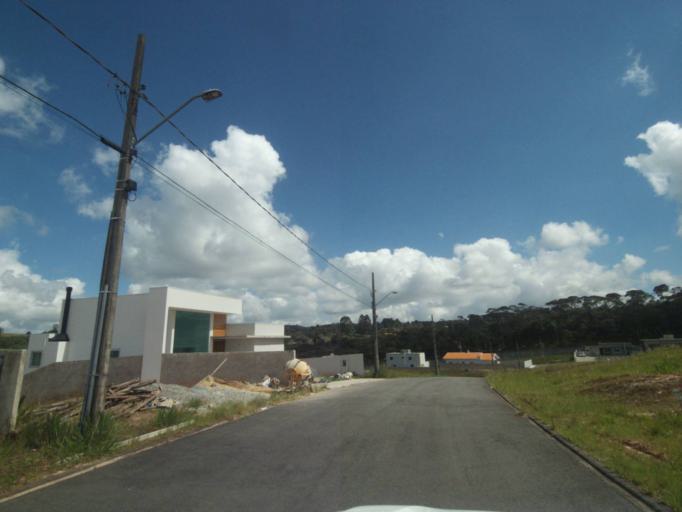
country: BR
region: Parana
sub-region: Colombo
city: Colombo
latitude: -25.3104
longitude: -49.2335
